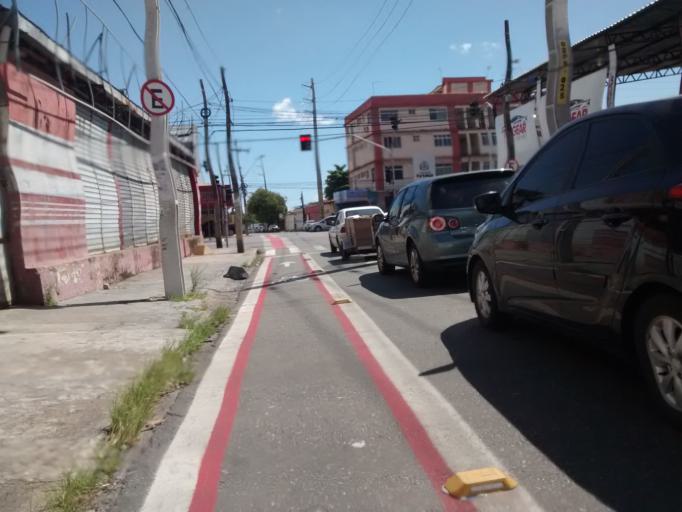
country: BR
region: Ceara
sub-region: Fortaleza
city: Fortaleza
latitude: -3.7347
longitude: -38.5575
